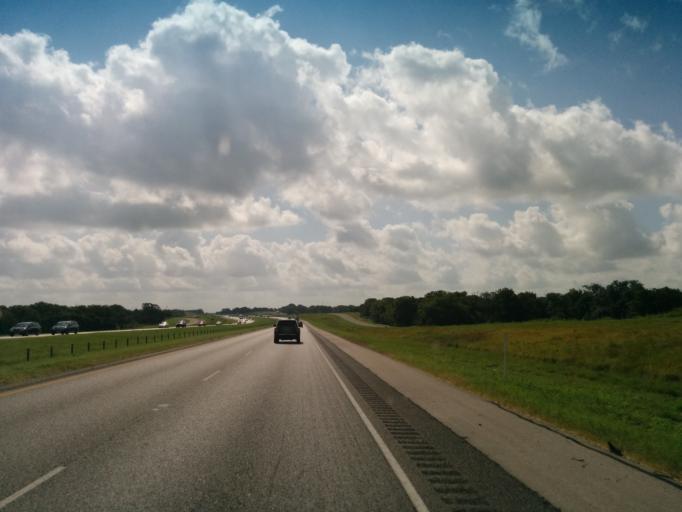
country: US
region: Texas
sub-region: Fayette County
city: Flatonia
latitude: 29.6923
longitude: -97.0130
